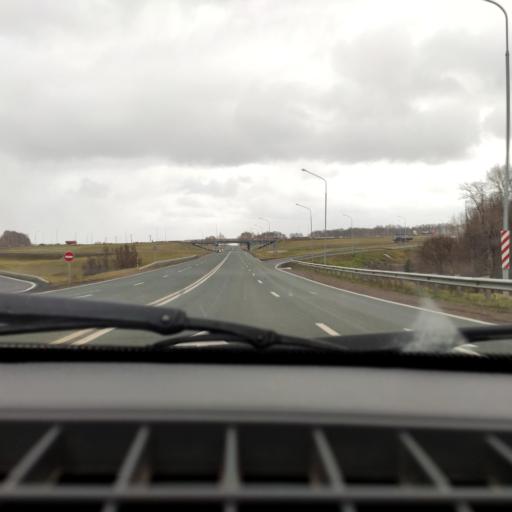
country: RU
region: Bashkortostan
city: Avdon
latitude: 54.6679
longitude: 55.7330
